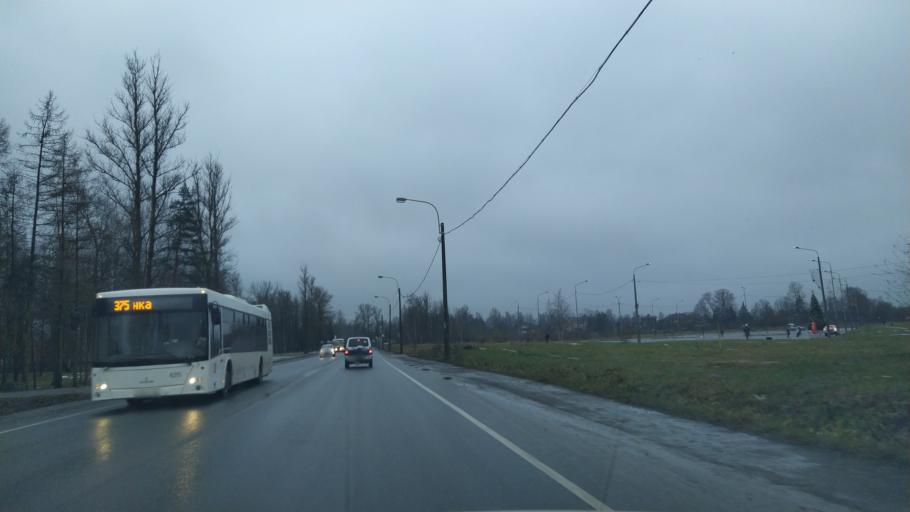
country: RU
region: St.-Petersburg
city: Tyarlevo
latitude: 59.7292
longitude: 30.4625
